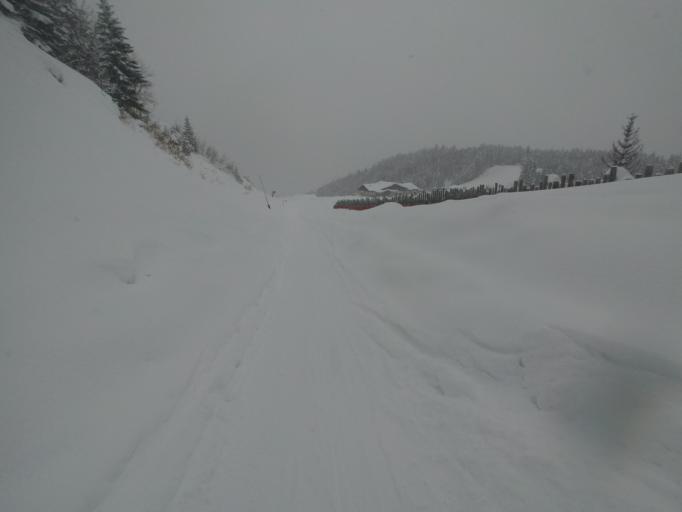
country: AT
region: Salzburg
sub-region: Politischer Bezirk Sankt Johann im Pongau
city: Sankt Johann im Pongau
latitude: 47.3166
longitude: 13.2225
